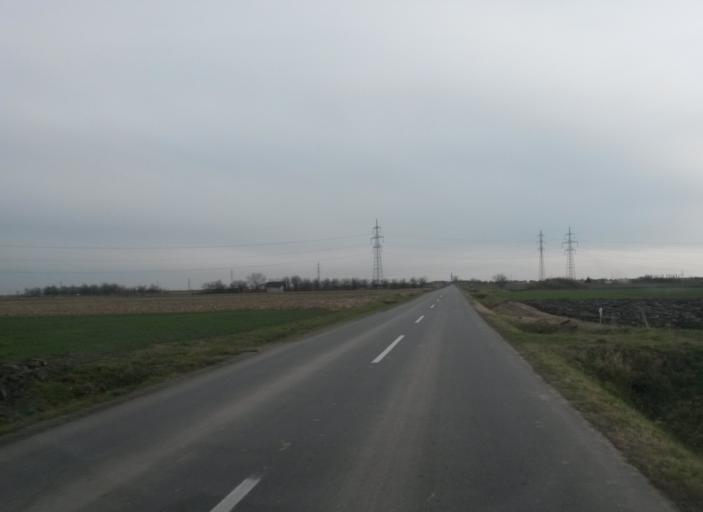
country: HR
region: Osjecko-Baranjska
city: Ovcara
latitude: 45.4960
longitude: 18.6182
